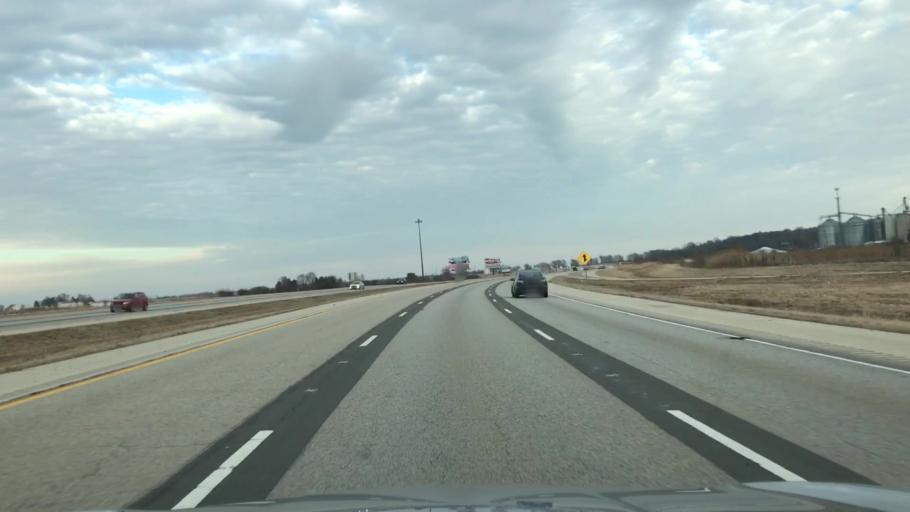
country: US
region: Illinois
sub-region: Sangamon County
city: Williamsville
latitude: 40.0224
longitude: -89.4935
